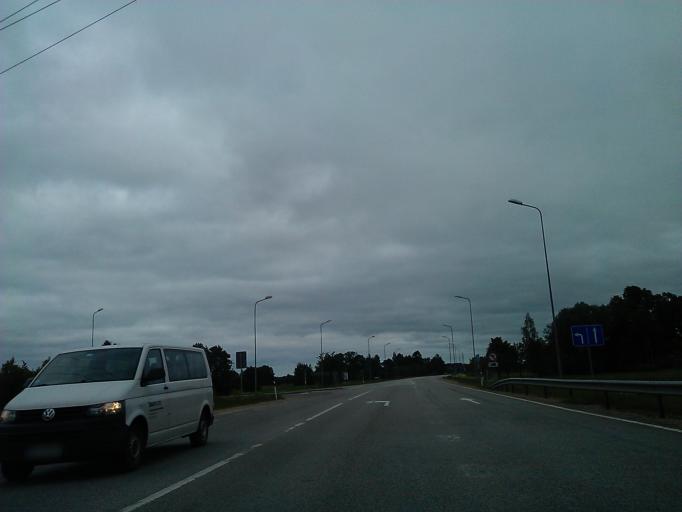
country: LV
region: Adazi
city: Adazi
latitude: 57.0999
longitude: 24.3121
